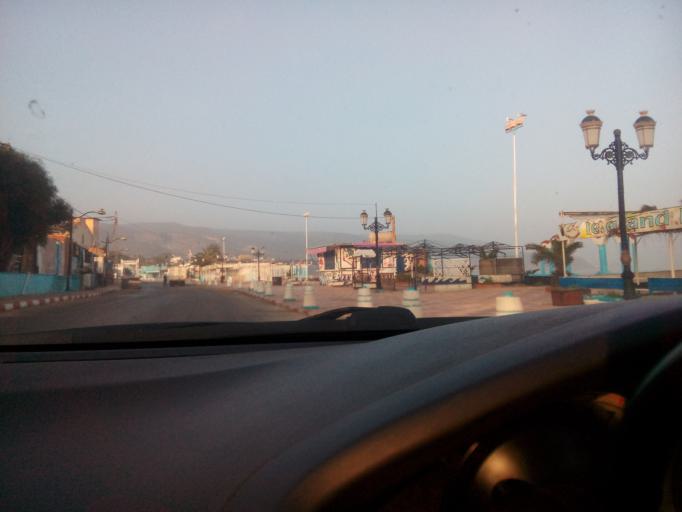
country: DZ
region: Oran
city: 'Ain el Turk
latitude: 35.7057
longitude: -0.8906
